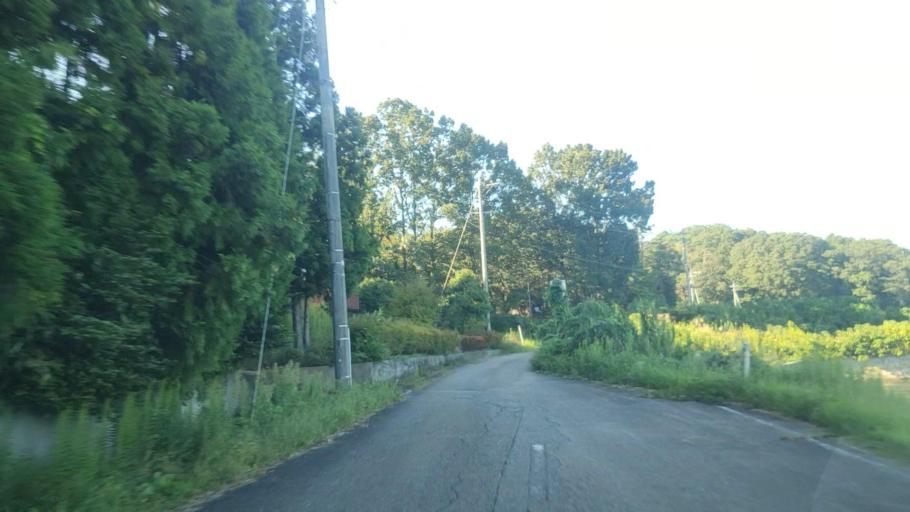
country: JP
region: Ishikawa
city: Nanao
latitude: 37.1226
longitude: 136.8948
